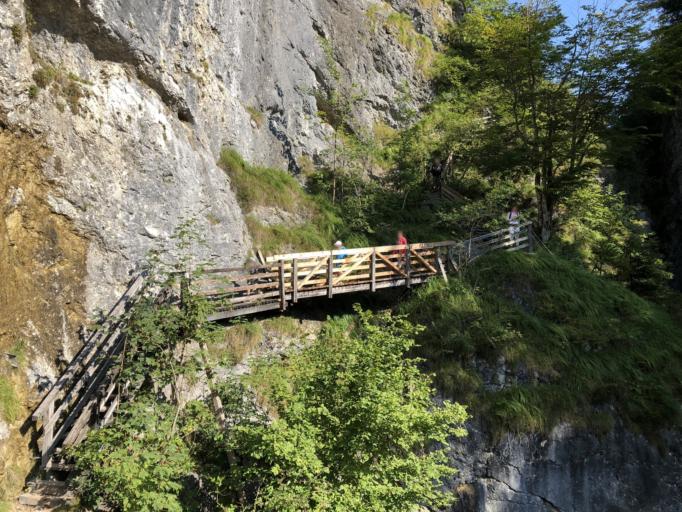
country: AT
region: Salzburg
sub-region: Politischer Bezirk Hallein
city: Scheffau am Tennengebirge
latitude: 47.5829
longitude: 13.2658
